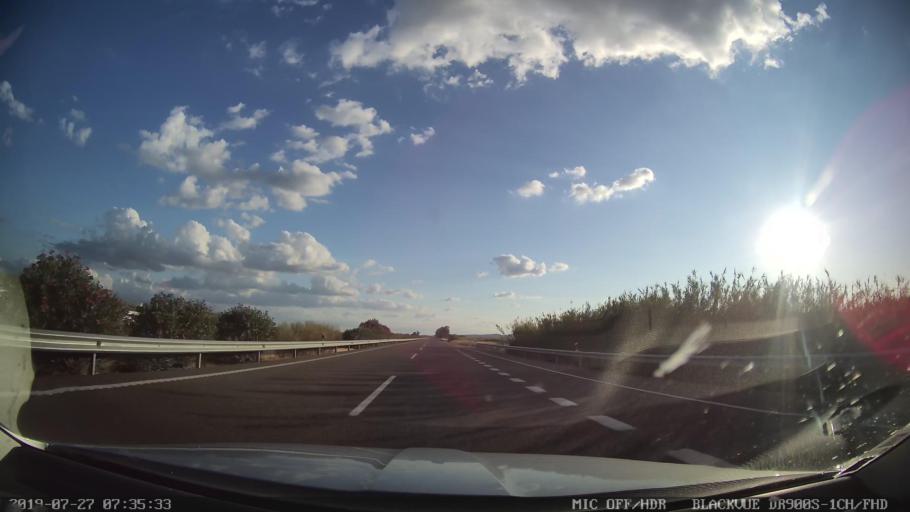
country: ES
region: Extremadura
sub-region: Provincia de Caceres
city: Miajadas
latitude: 39.1139
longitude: -5.9802
